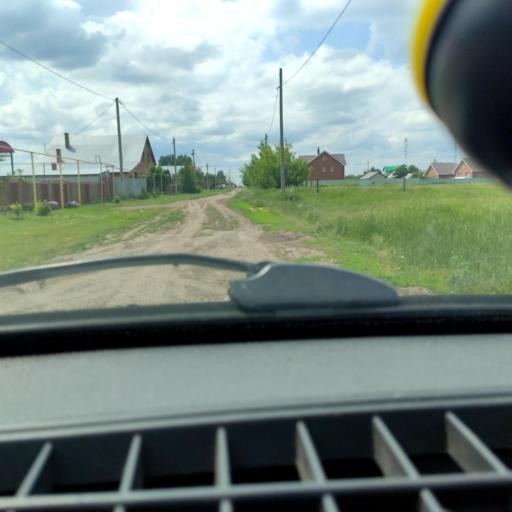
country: RU
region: Samara
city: Povolzhskiy
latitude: 53.6482
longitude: 49.6927
